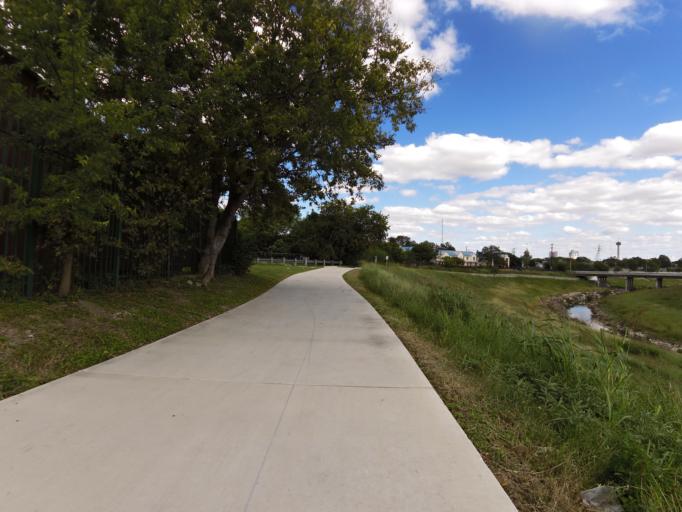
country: US
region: Texas
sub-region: Bexar County
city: San Antonio
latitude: 29.4146
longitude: -98.5171
